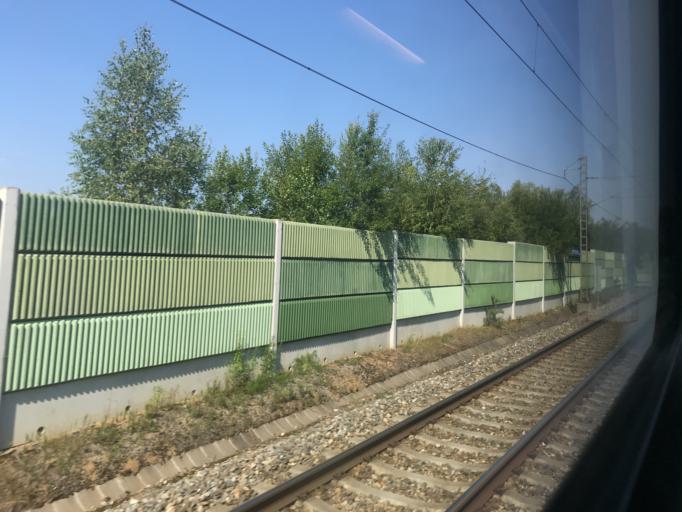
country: CZ
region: Central Bohemia
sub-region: Okres Praha-Vychod
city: Mnichovice
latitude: 49.9080
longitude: 14.7237
